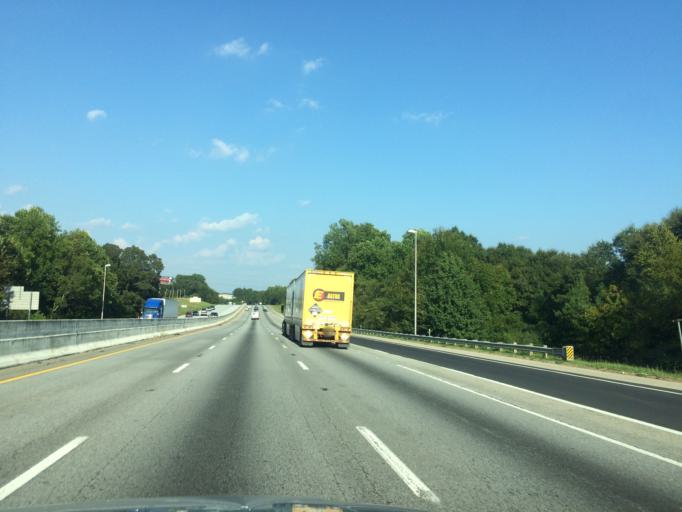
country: US
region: South Carolina
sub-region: Anderson County
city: Northlake
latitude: 34.6336
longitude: -82.5961
